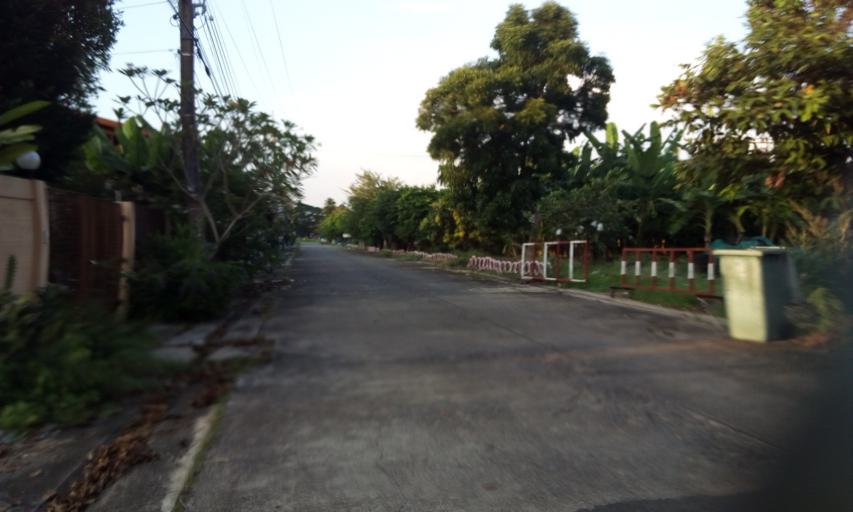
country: TH
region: Pathum Thani
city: Ban Rangsit
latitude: 14.0494
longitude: 100.8225
